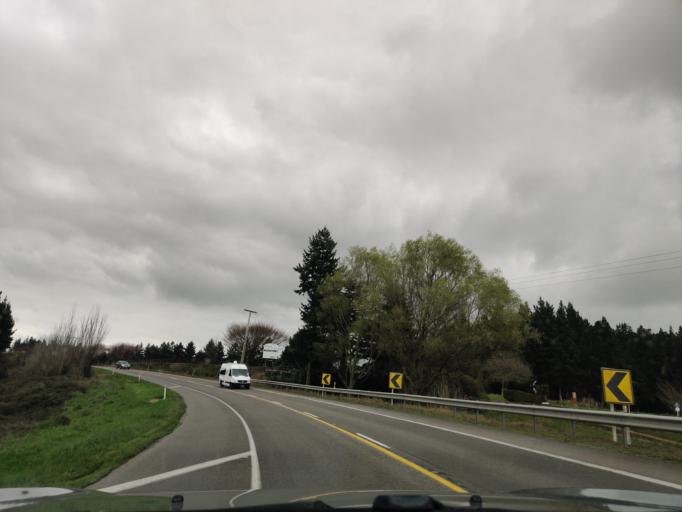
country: NZ
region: Manawatu-Wanganui
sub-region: Palmerston North City
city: Palmerston North
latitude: -40.2286
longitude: 176.0671
